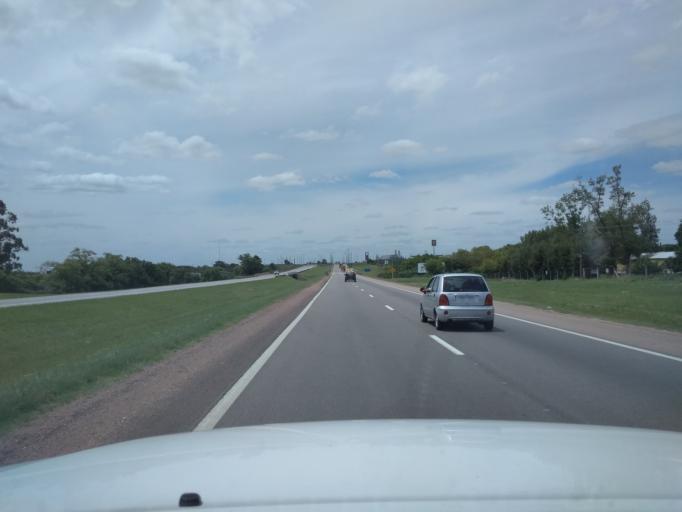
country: UY
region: Canelones
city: La Paz
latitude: -34.7559
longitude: -56.2587
